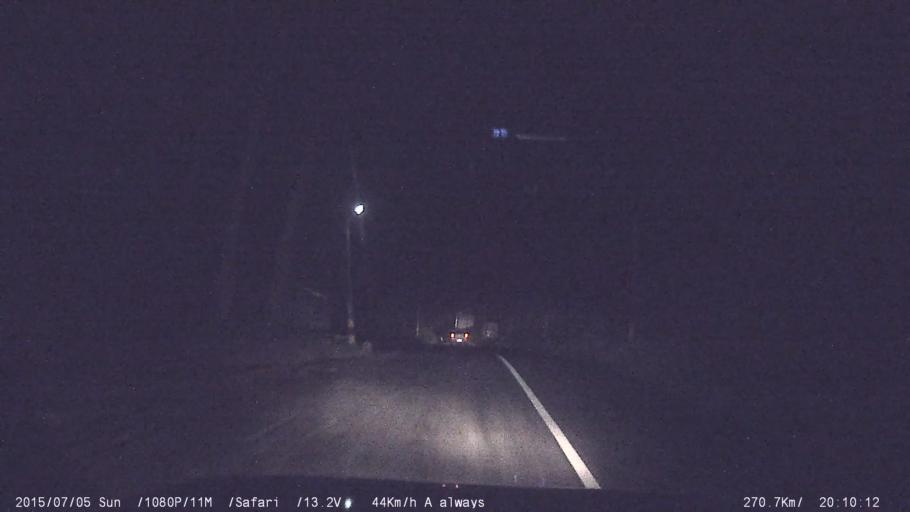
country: IN
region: Kerala
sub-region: Palakkad district
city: Palakkad
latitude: 10.8495
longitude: 76.5780
